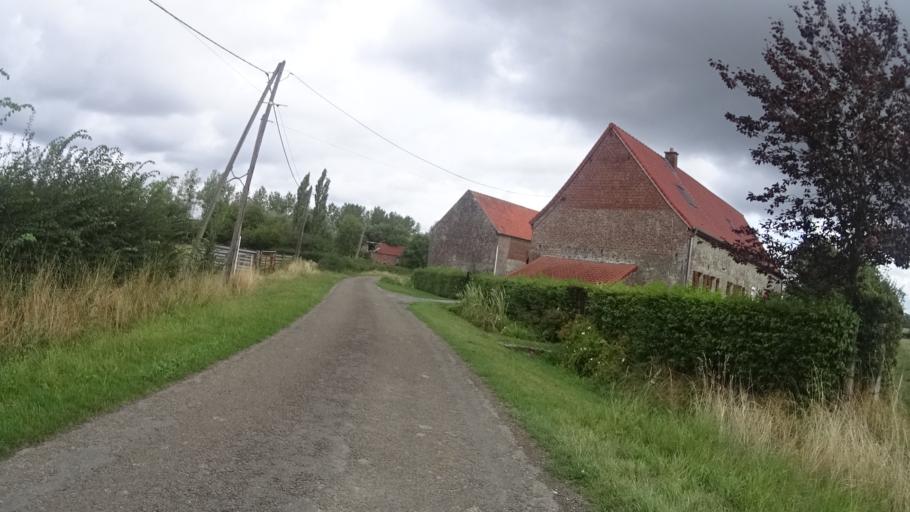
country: FR
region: Nord-Pas-de-Calais
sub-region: Departement du Nord
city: Landrecies
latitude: 50.1280
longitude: 3.7195
